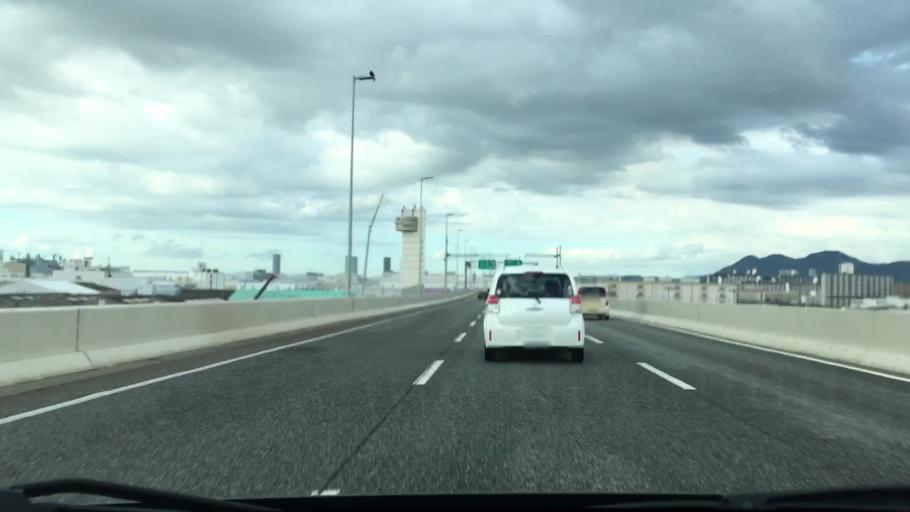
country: JP
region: Fukuoka
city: Fukuoka-shi
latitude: 33.6185
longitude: 130.4123
